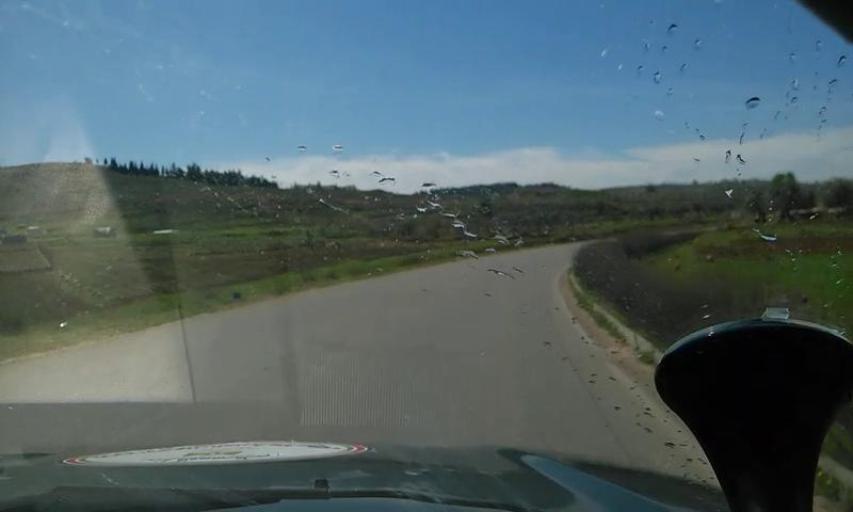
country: PS
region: West Bank
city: Al Jib
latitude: 31.8430
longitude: 35.1764
